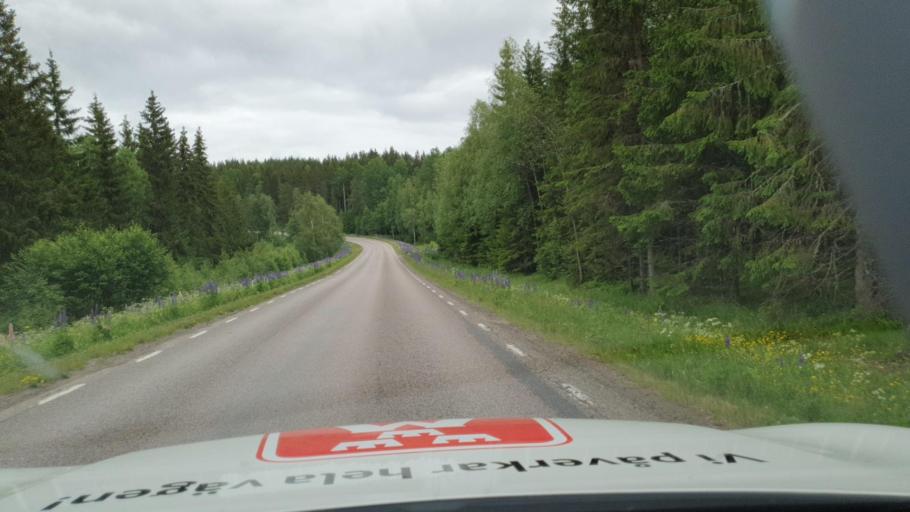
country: SE
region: Vaermland
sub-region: Torsby Kommun
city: Torsby
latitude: 59.9310
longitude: 12.8051
